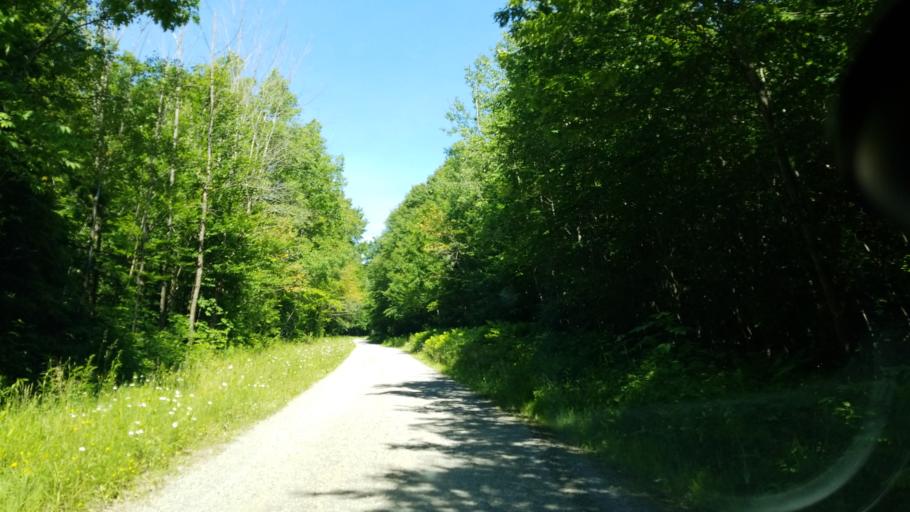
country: US
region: Pennsylvania
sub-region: Clearfield County
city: Clearfield
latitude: 41.2192
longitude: -78.3896
